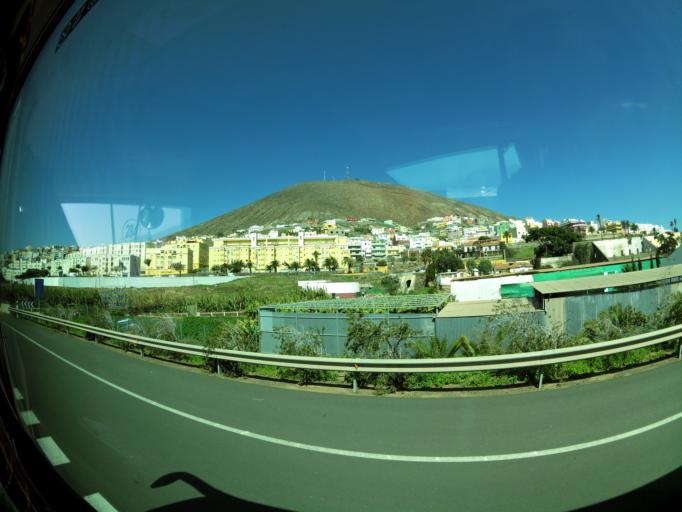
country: ES
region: Canary Islands
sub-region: Provincia de Las Palmas
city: Guia
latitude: 28.1437
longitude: -15.6411
